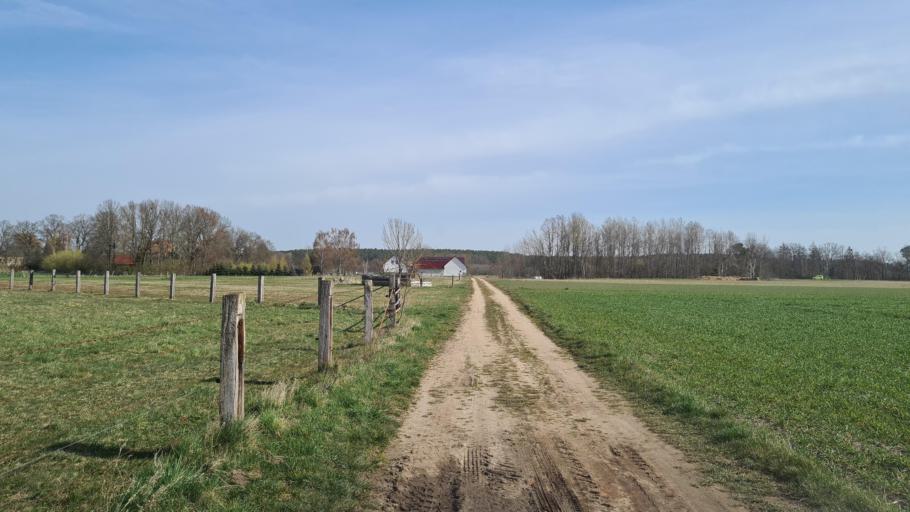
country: DE
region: Brandenburg
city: Sonnewalde
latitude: 51.7164
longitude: 13.6507
